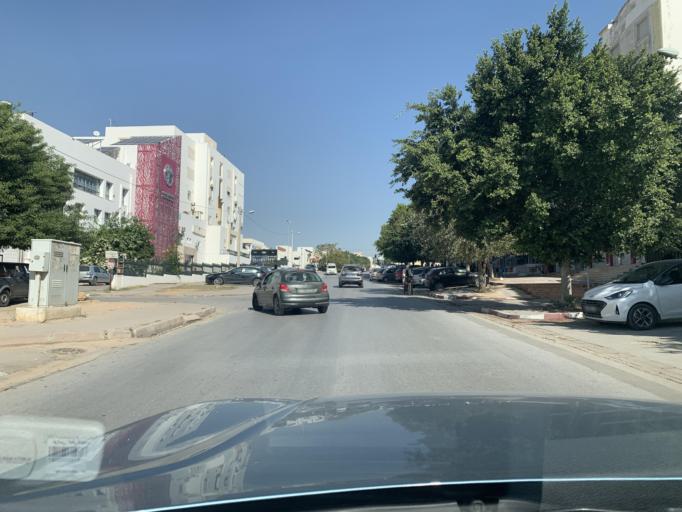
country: TN
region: Manouba
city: Manouba
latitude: 36.8297
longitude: 10.1225
